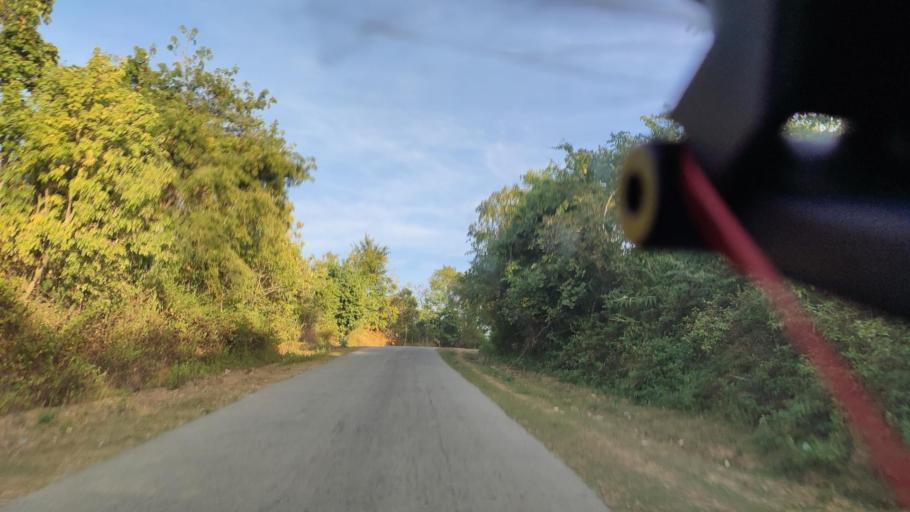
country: MM
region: Mandalay
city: Nay Pyi Taw
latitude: 19.9925
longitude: 95.9386
